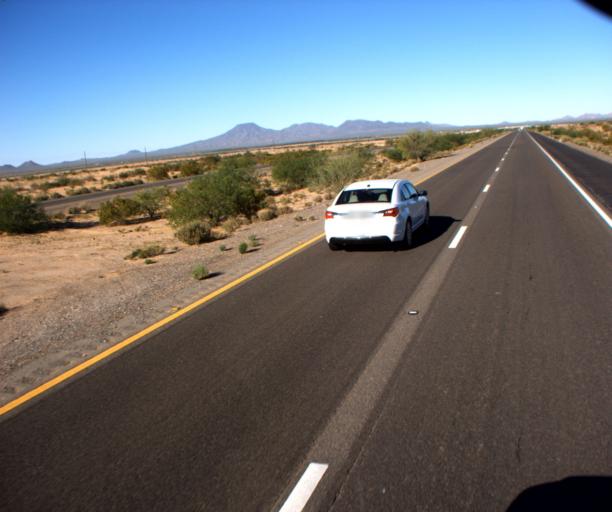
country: US
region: Arizona
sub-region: Pinal County
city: Casa Grande
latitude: 32.8284
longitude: -111.9292
